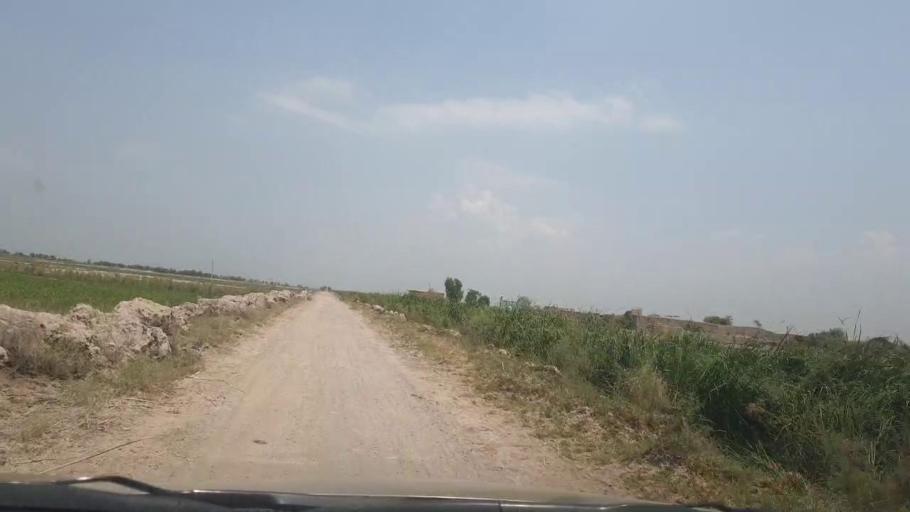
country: PK
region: Sindh
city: Ratodero
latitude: 27.7182
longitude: 68.2934
